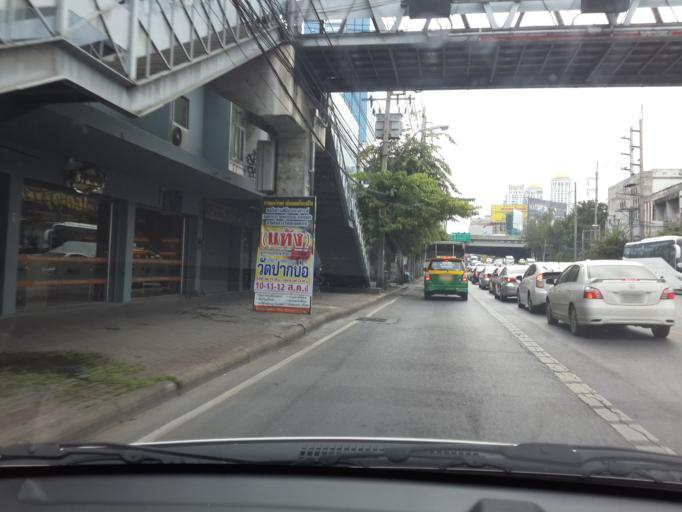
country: TH
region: Bangkok
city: Din Daeng
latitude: 13.7498
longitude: 100.5516
